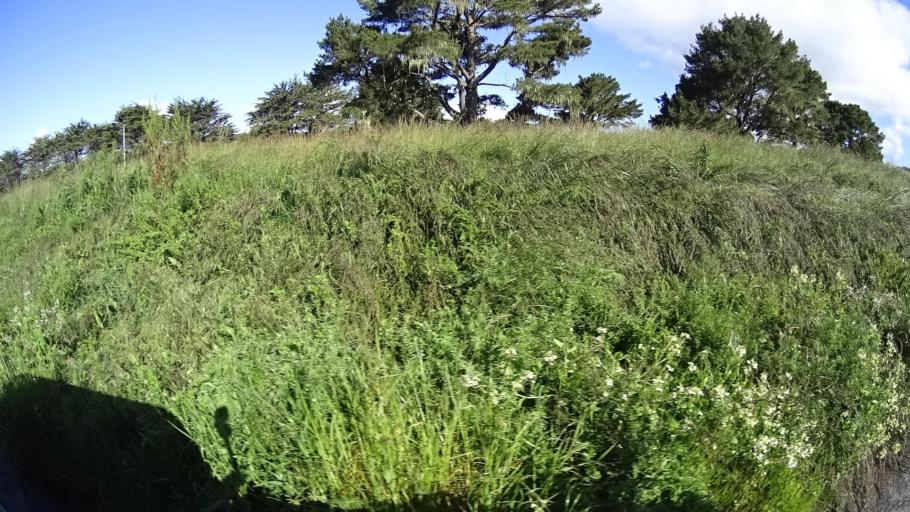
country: US
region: California
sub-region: Humboldt County
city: Westhaven-Moonstone
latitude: 41.0126
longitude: -124.1076
